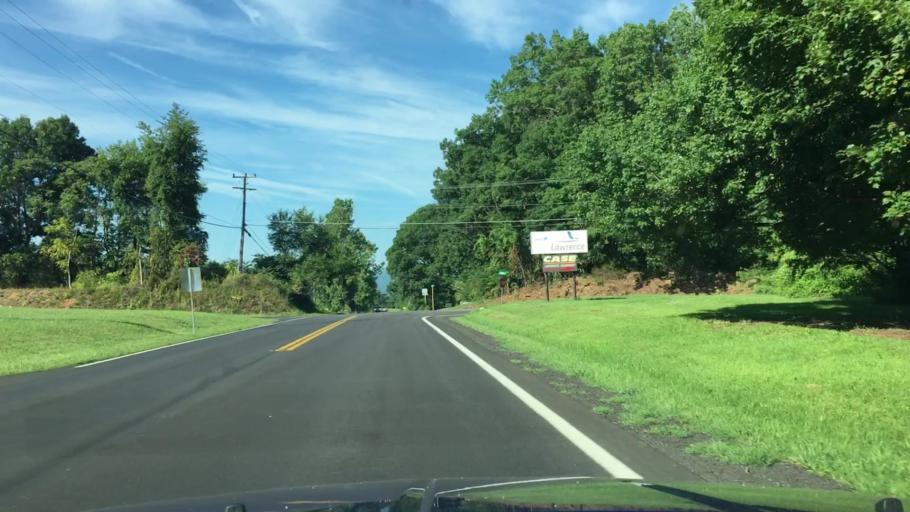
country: US
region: Virginia
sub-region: Augusta County
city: Lyndhurst
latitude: 38.0342
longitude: -78.9228
